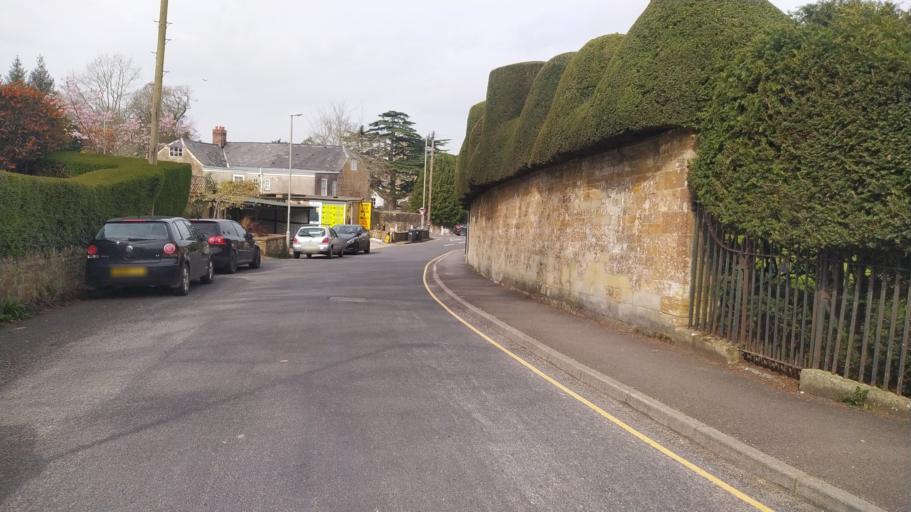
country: GB
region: England
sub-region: Dorset
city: Beaminster
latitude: 50.8075
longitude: -2.7366
